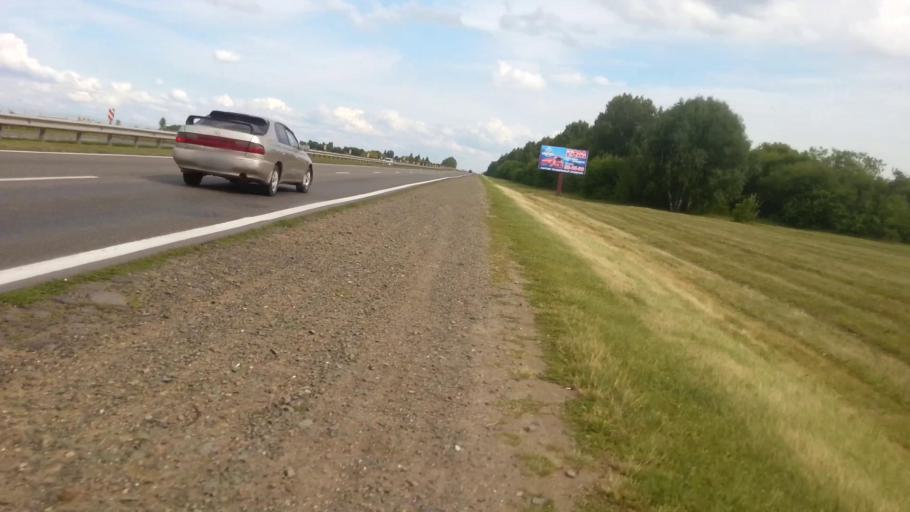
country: RU
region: Altai Krai
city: Nauchnyy Gorodok
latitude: 53.3560
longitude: 83.5158
